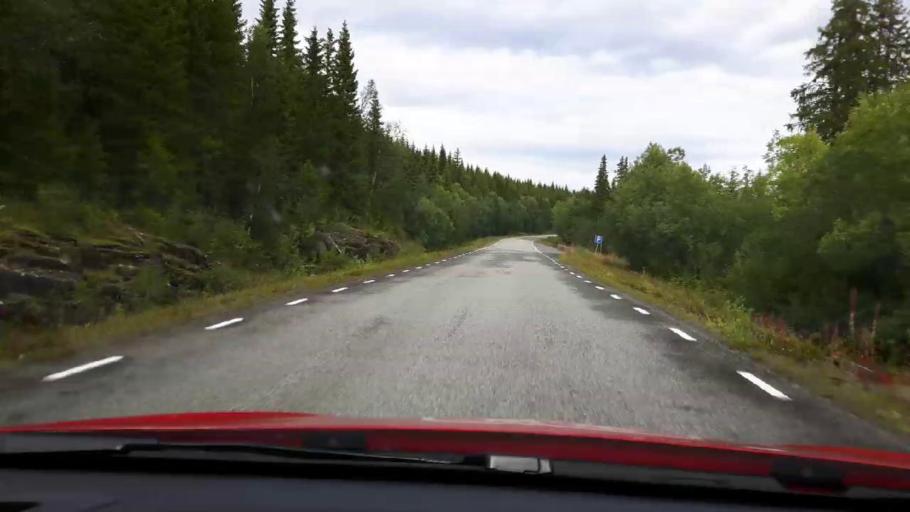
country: SE
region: Jaemtland
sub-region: Are Kommun
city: Are
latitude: 63.7201
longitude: 12.9681
